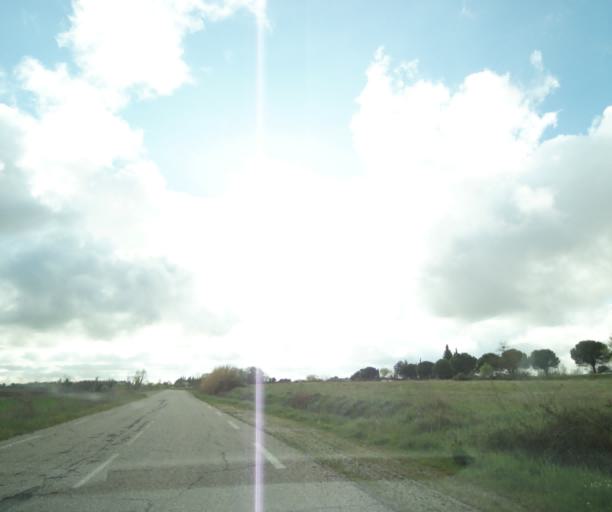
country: FR
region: Languedoc-Roussillon
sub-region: Departement de l'Herault
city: Laverune
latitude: 43.5861
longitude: 3.7945
